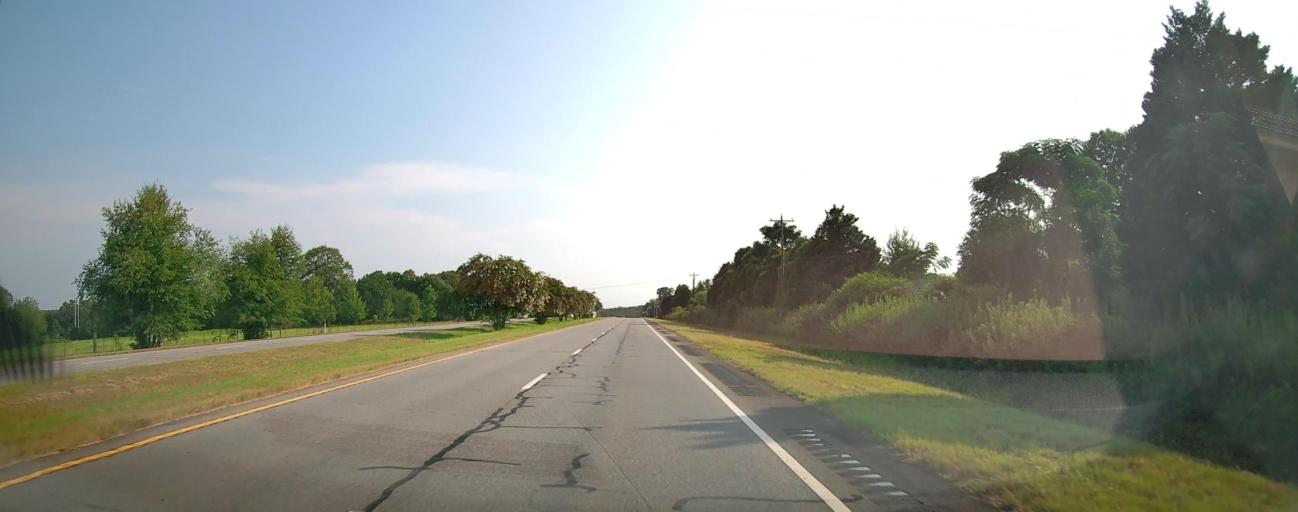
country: US
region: Georgia
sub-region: Peach County
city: Byron
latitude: 32.6301
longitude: -83.7824
